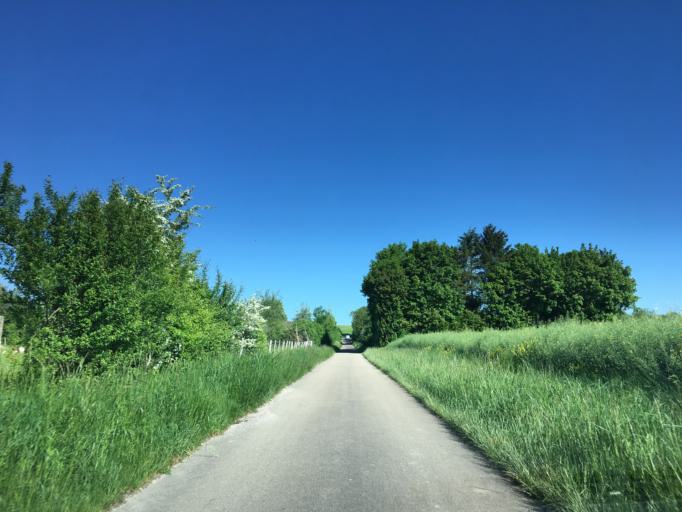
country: FR
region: Bourgogne
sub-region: Departement de l'Yonne
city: Aillant-sur-Tholon
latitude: 47.8257
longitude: 3.3427
